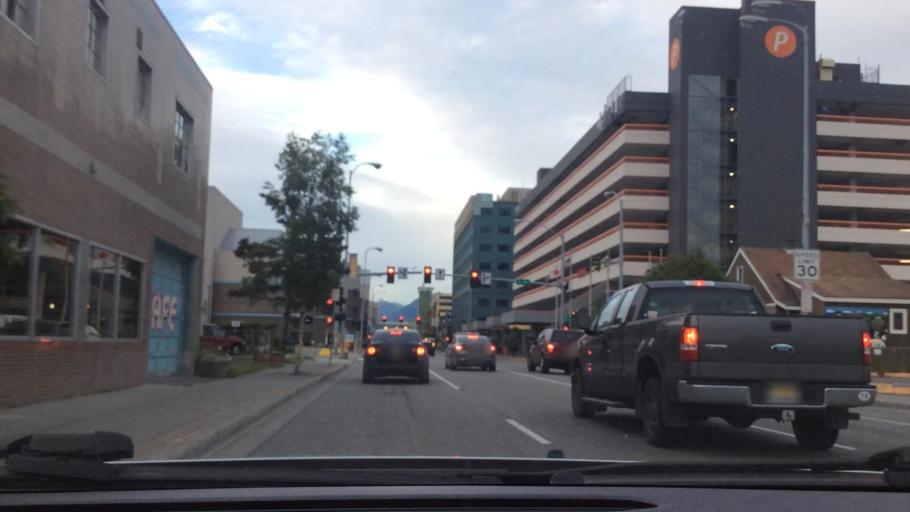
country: US
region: Alaska
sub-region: Anchorage Municipality
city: Anchorage
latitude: 61.2167
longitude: -149.8987
